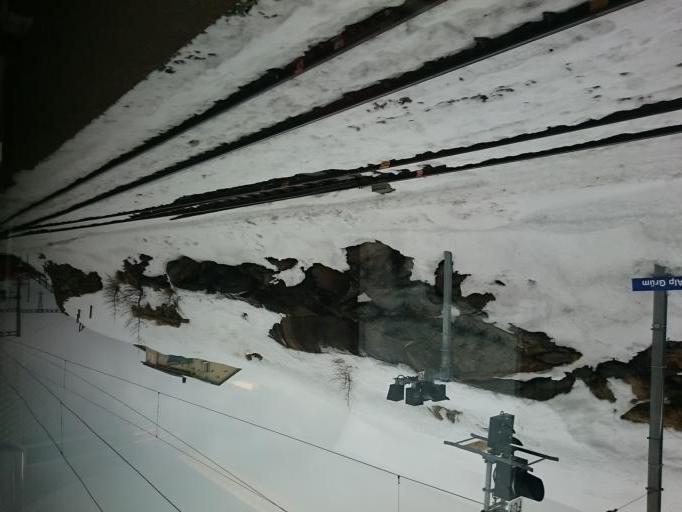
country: CH
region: Grisons
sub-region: Bernina District
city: Poschiavo
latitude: 46.3745
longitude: 10.0314
